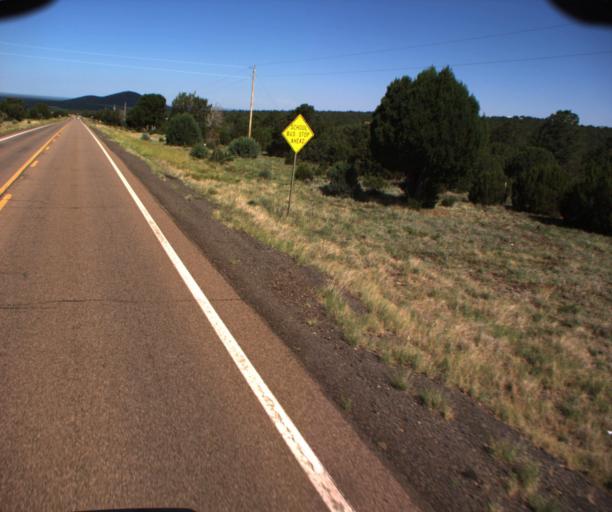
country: US
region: Arizona
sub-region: Navajo County
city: White Mountain Lake
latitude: 34.2809
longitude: -109.8063
